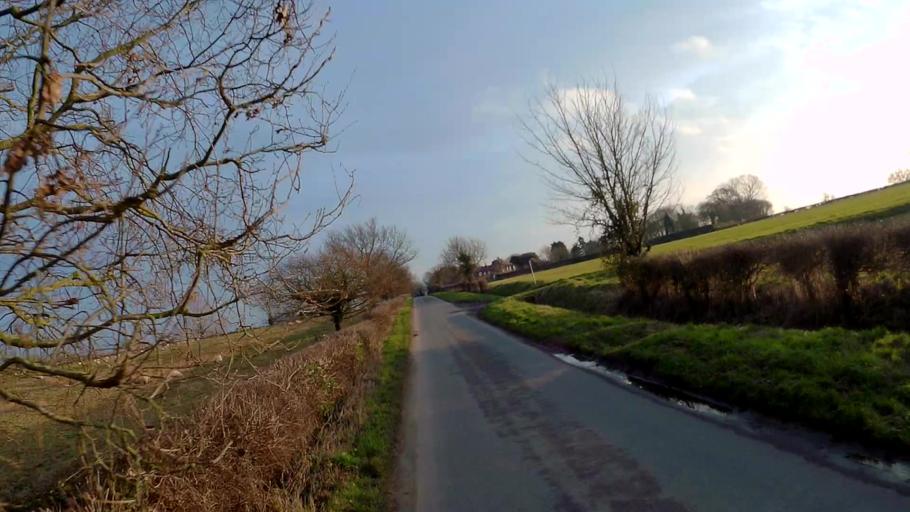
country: GB
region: England
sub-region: Lincolnshire
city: Bourne
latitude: 52.8072
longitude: -0.3960
